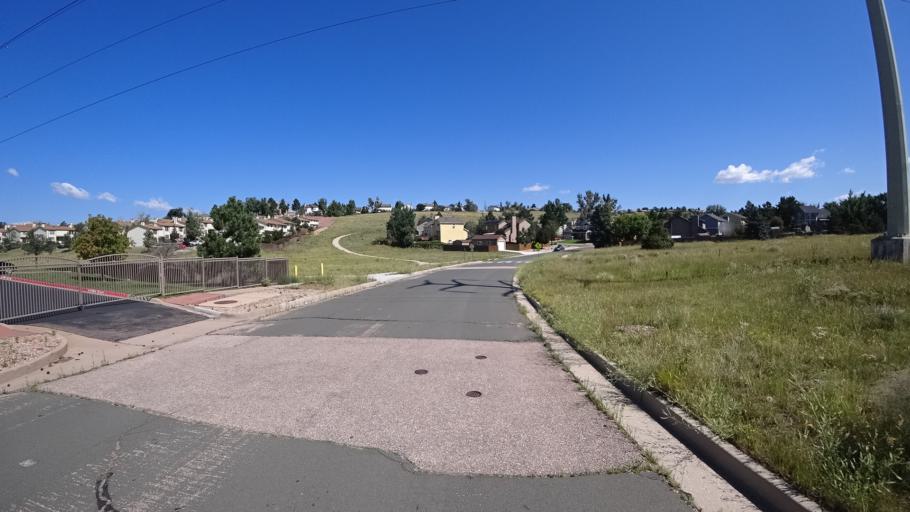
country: US
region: Colorado
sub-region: El Paso County
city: Black Forest
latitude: 38.9404
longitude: -104.7521
